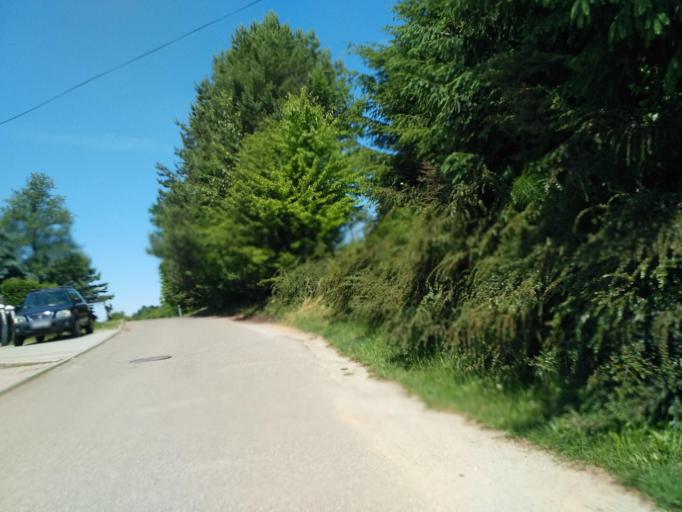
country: PL
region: Subcarpathian Voivodeship
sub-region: Krosno
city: Krosno
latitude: 49.7047
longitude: 21.7707
